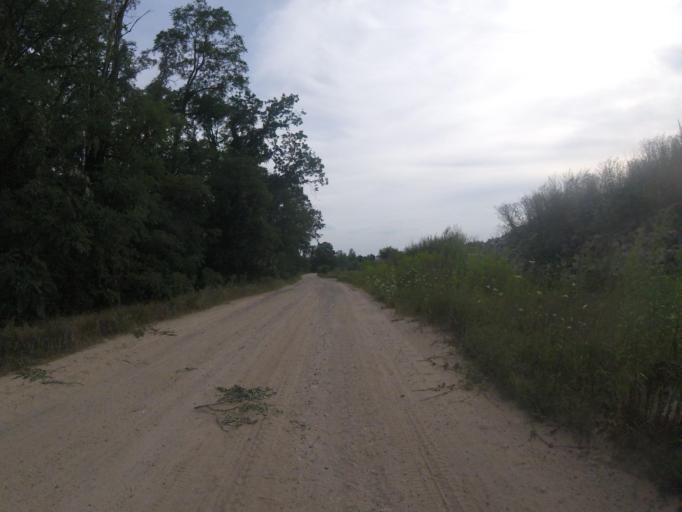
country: DE
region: Brandenburg
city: Rangsdorf
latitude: 52.2787
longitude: 13.4752
